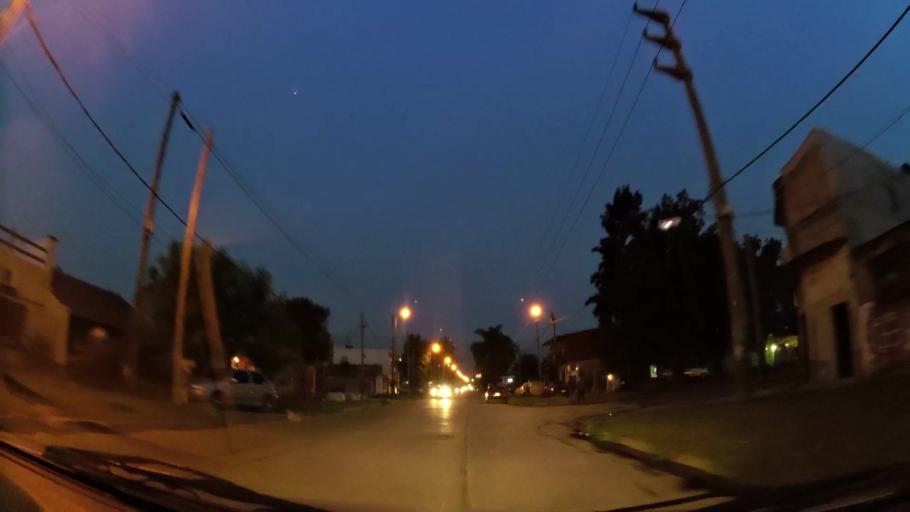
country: AR
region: Buenos Aires
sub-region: Partido de Lanus
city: Lanus
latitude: -34.7400
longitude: -58.3551
